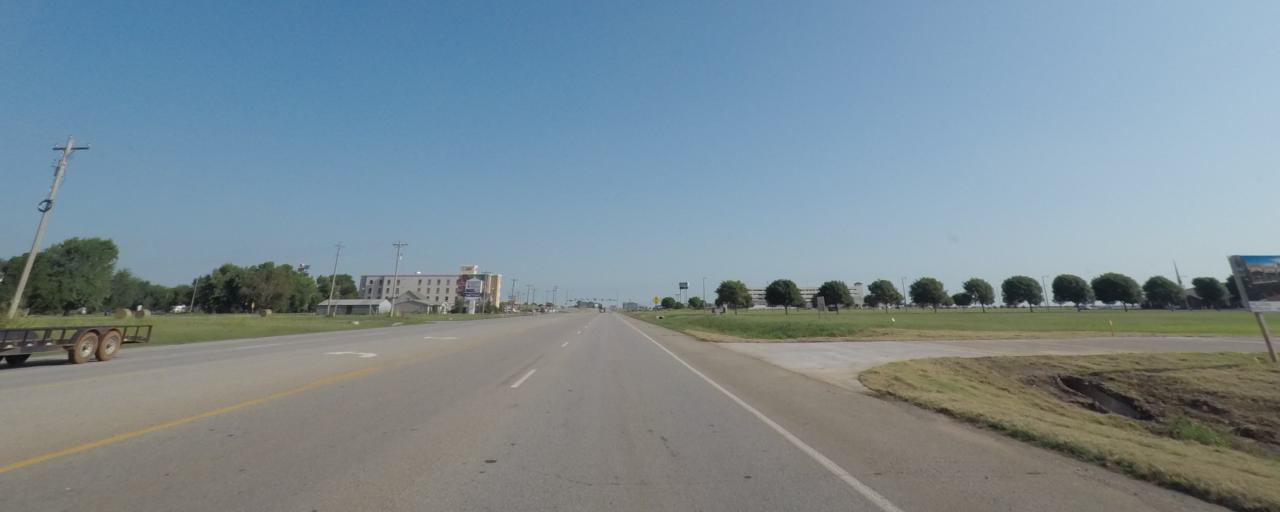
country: US
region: Oklahoma
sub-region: McClain County
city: Newcastle
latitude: 35.2726
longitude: -97.6001
